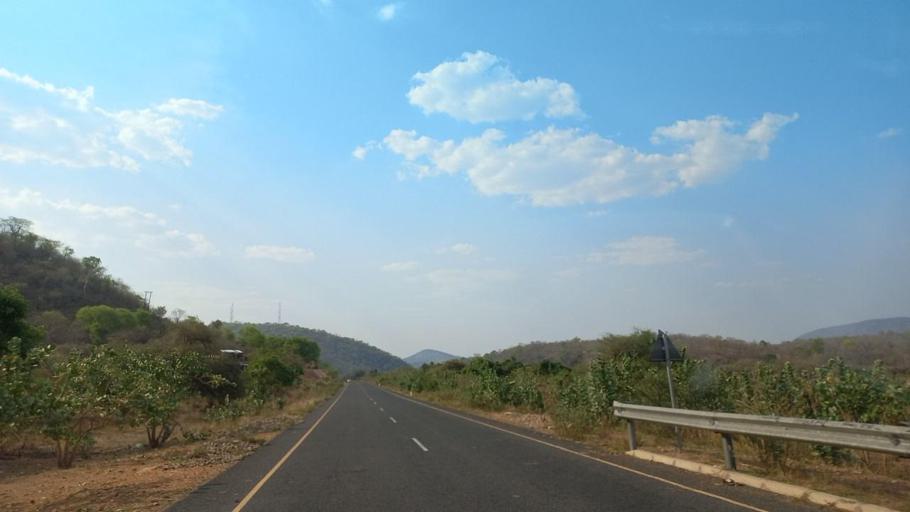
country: ZM
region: Lusaka
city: Luangwa
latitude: -15.0168
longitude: 30.2225
